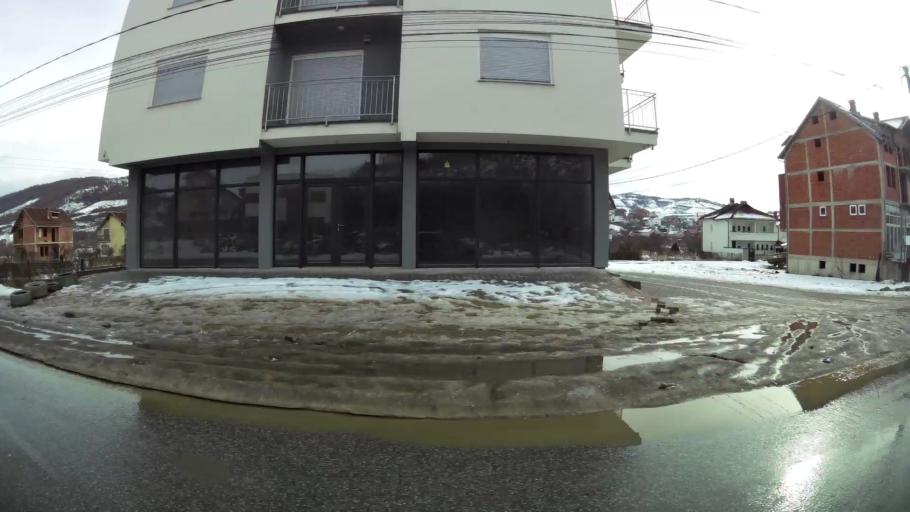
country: XK
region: Pristina
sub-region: Komuna e Prishtines
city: Pristina
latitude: 42.6890
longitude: 21.1783
